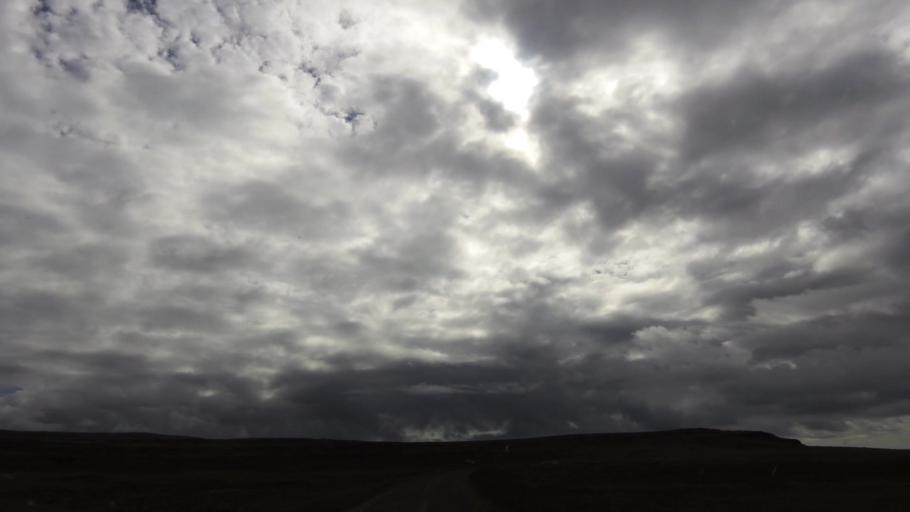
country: IS
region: West
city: Olafsvik
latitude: 65.6082
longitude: -24.3338
